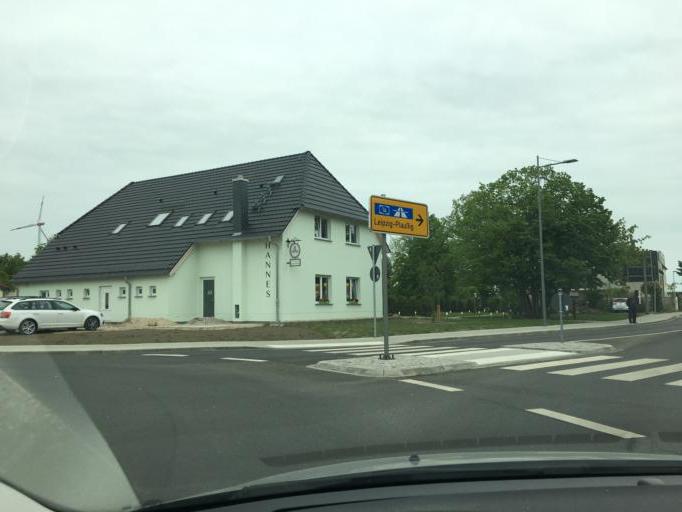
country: DE
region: Saxony
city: Rackwitz
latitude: 51.4062
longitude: 12.4187
